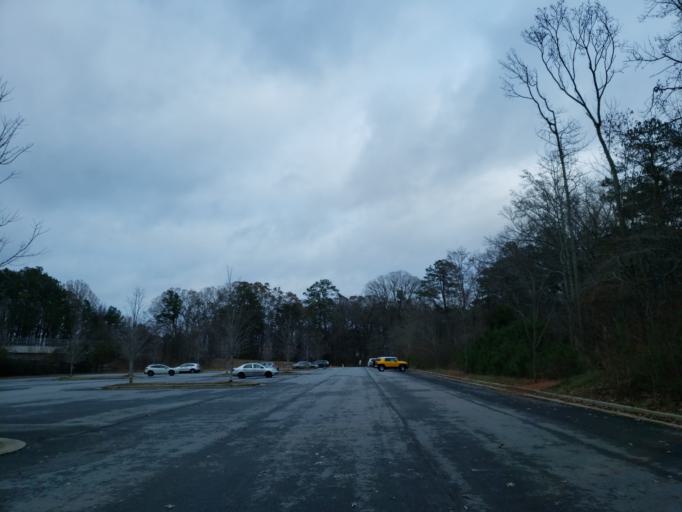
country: US
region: Georgia
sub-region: Cobb County
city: Marietta
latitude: 33.9847
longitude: -84.5832
